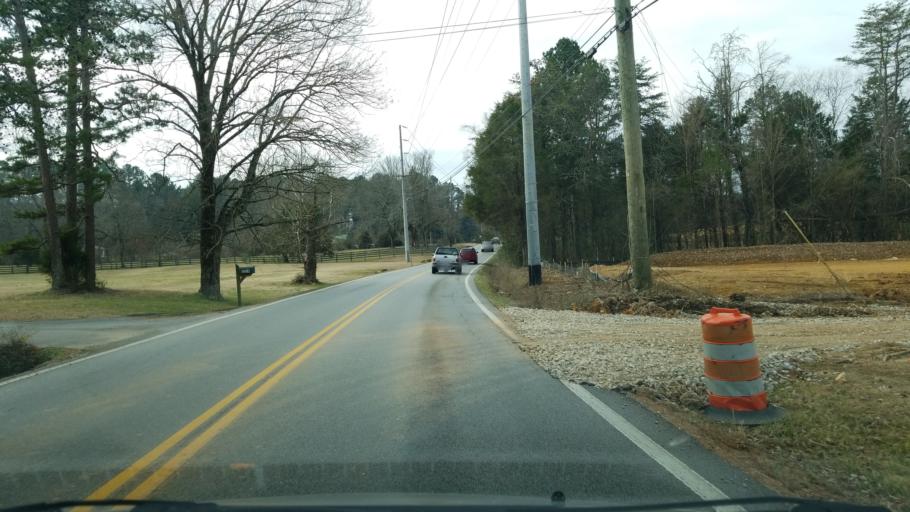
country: US
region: Tennessee
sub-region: Hamilton County
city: Collegedale
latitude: 35.0379
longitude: -85.0768
